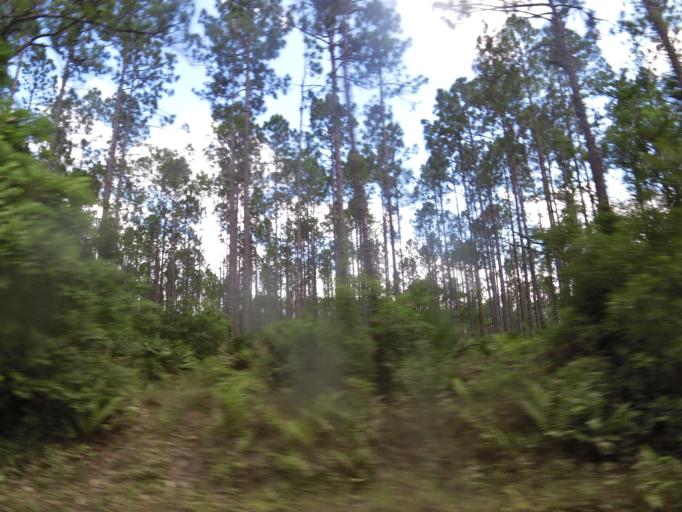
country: US
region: Florida
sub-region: Clay County
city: Asbury Lake
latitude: 29.8960
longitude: -81.8592
